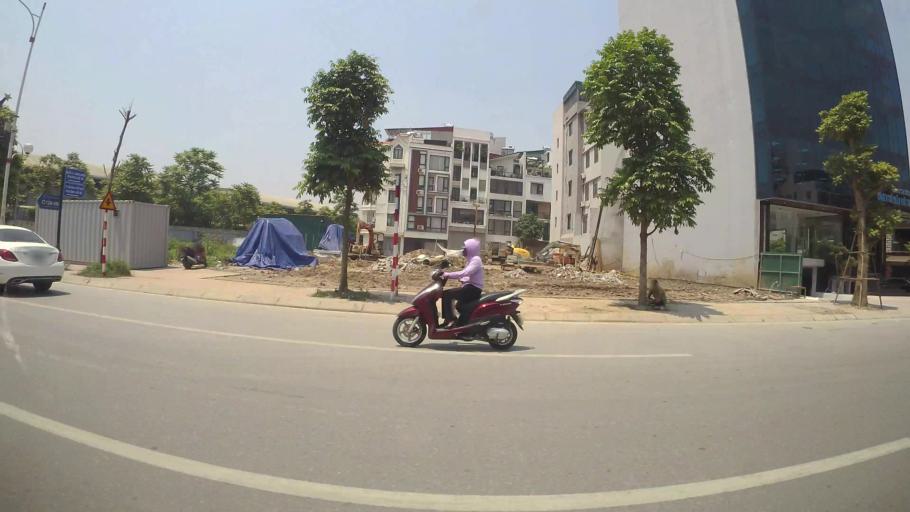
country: VN
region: Ha Noi
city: Hoan Kiem
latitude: 21.0405
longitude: 105.8745
